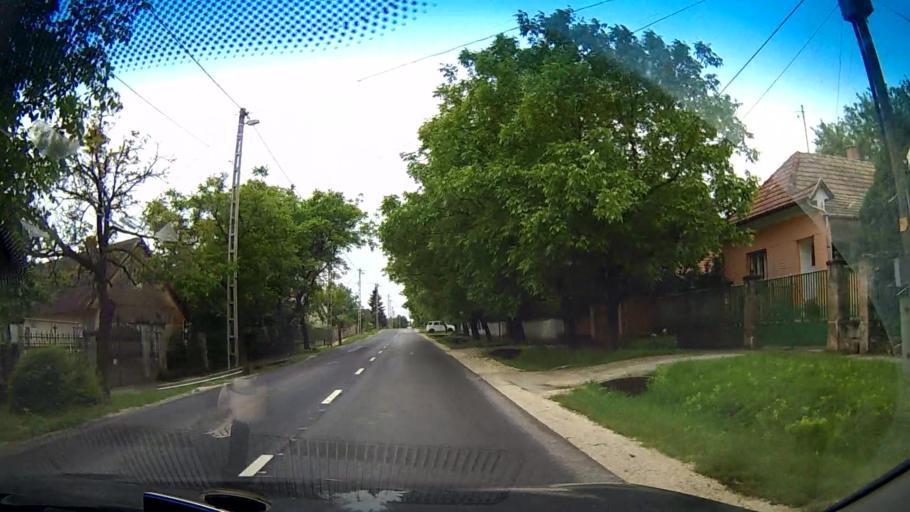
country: HU
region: Pest
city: Zsambek
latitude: 47.5633
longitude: 18.7306
